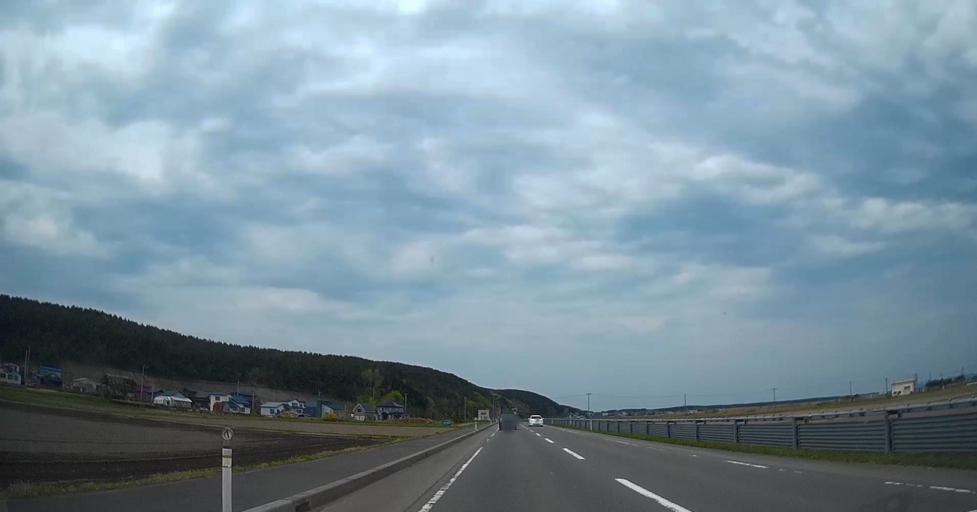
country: JP
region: Aomori
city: Shimokizukuri
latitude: 40.9936
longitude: 140.3590
